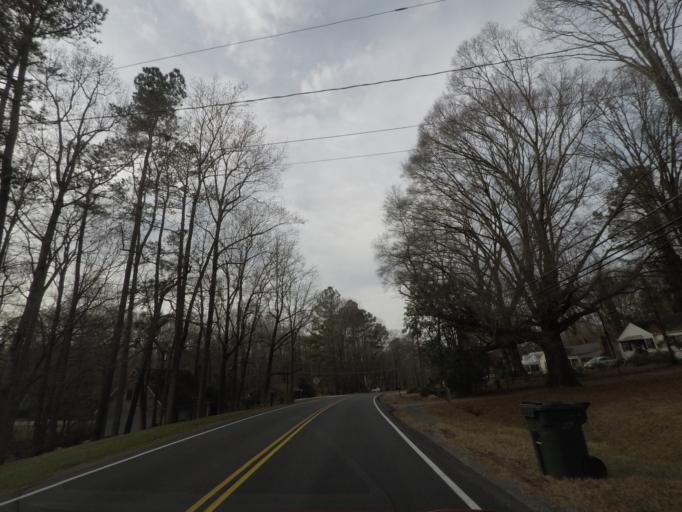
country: US
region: North Carolina
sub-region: Durham County
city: Durham
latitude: 36.0454
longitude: -78.9668
